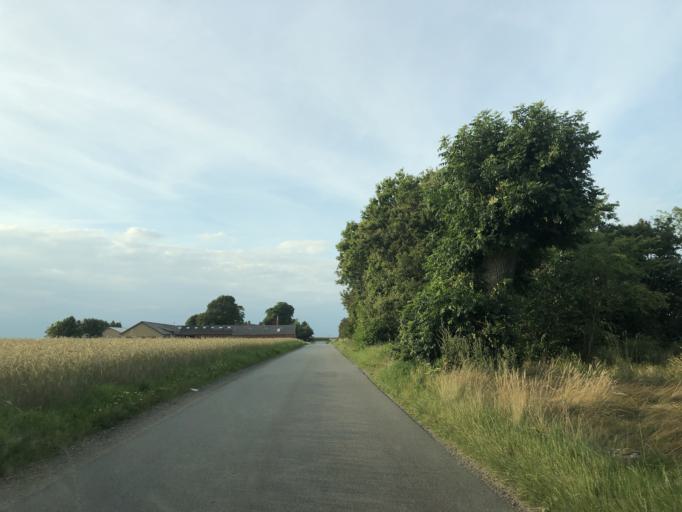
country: DK
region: South Denmark
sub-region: Vejle Kommune
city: Borkop
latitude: 55.6127
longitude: 9.6095
